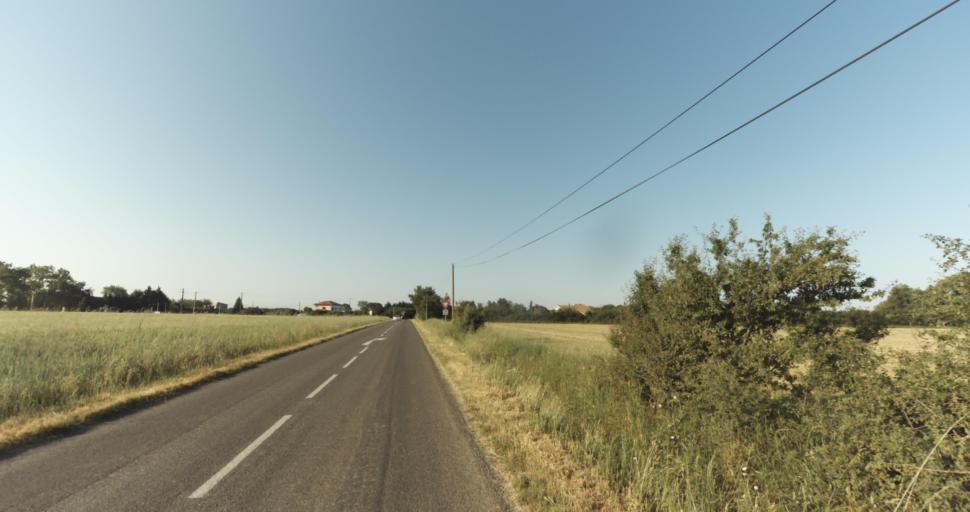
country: FR
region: Midi-Pyrenees
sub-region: Departement de la Haute-Garonne
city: Leguevin
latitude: 43.5776
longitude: 1.2361
